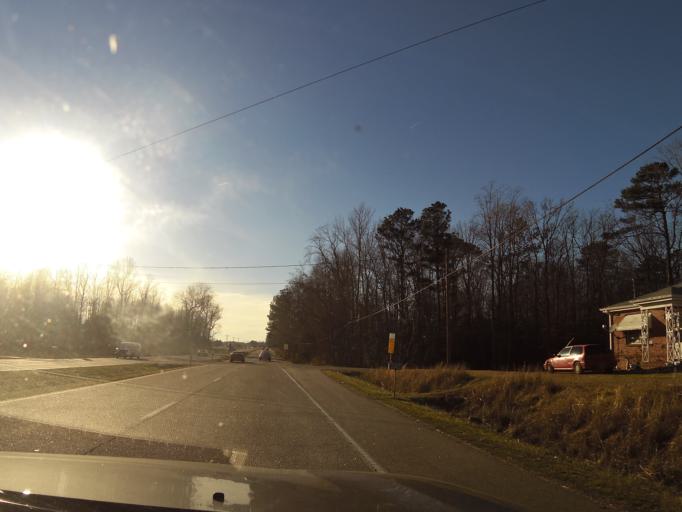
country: US
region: Virginia
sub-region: Isle of Wight County
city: Windsor
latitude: 36.6909
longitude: -76.7470
